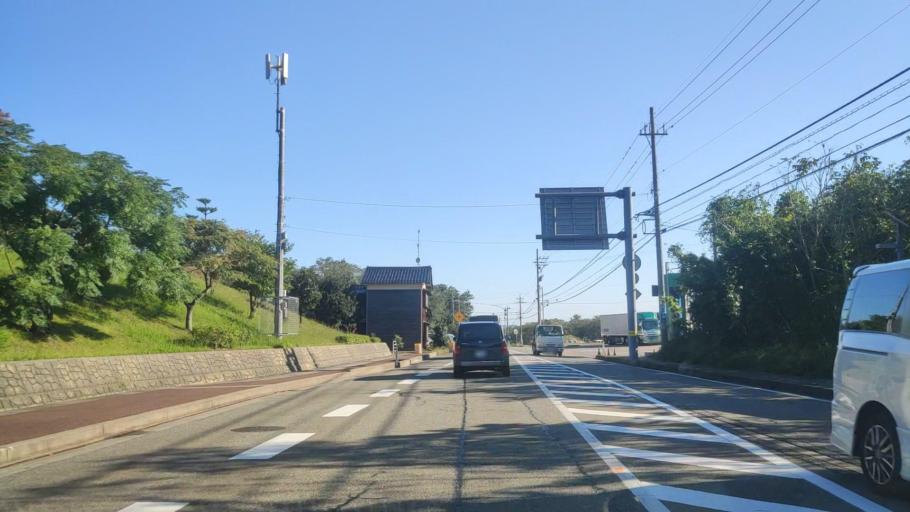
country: JP
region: Ishikawa
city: Tsubata
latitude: 36.7798
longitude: 136.7353
